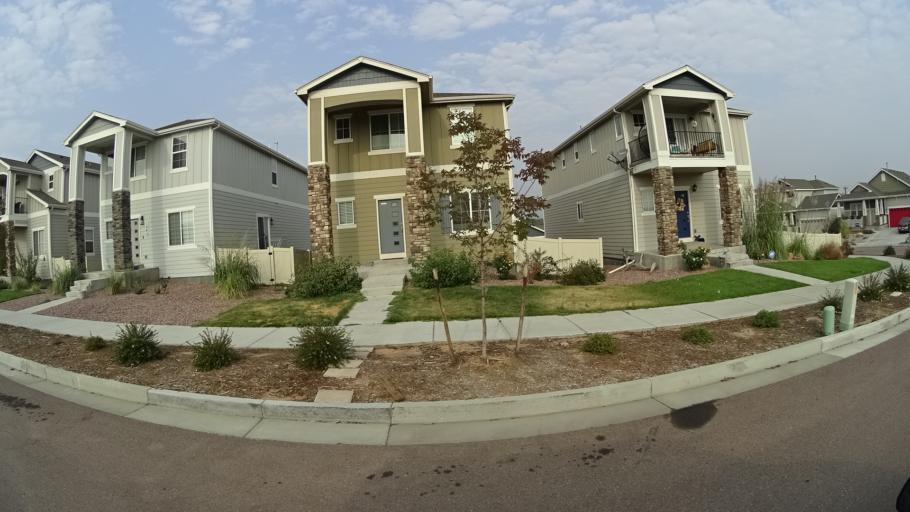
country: US
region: Colorado
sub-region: El Paso County
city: Stratmoor
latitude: 38.8137
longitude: -104.7829
